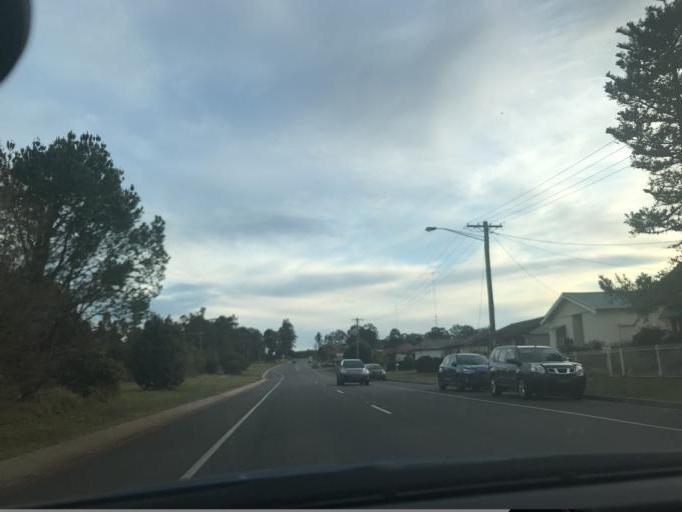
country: AU
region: New South Wales
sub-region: Cessnock
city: Cessnock
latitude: -32.8607
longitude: 151.3197
